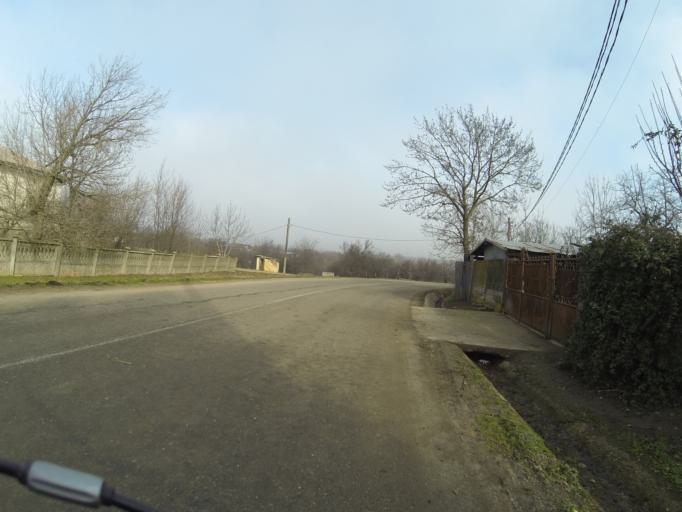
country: RO
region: Mehedinti
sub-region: Comuna Balacita
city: Balacita
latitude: 44.3849
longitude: 23.1270
